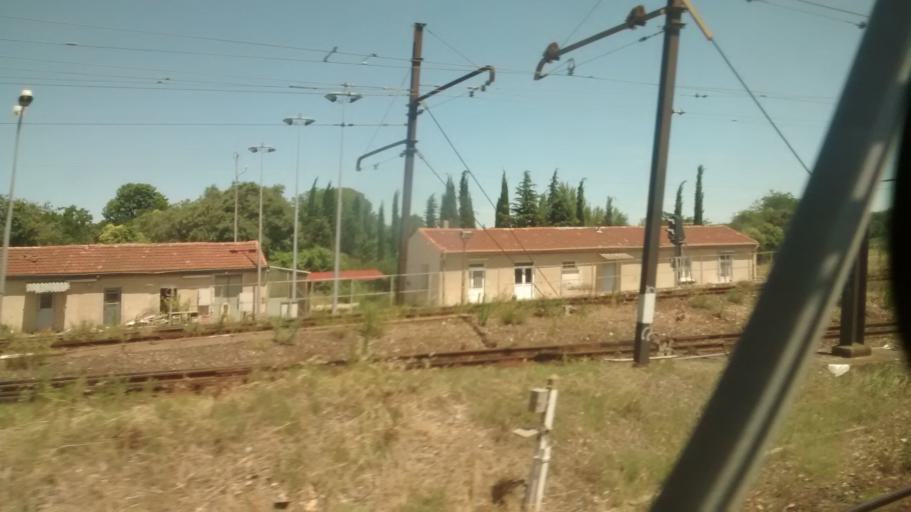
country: FR
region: Languedoc-Roussillon
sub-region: Departement du Gard
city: Rodilhan
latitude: 43.8454
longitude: 4.4144
